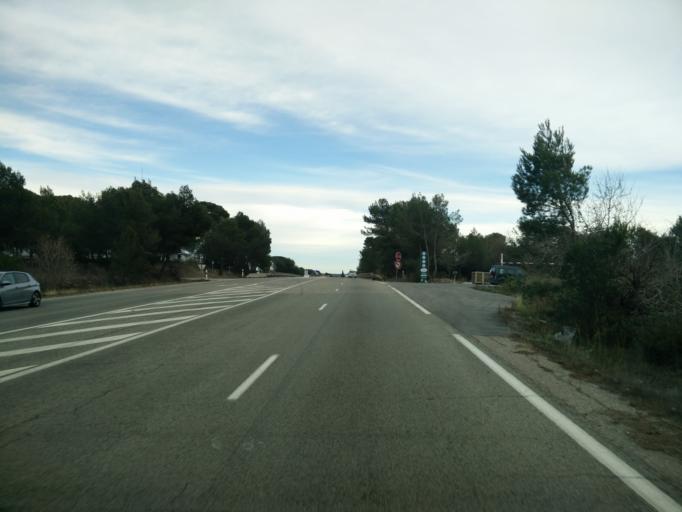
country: FR
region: Provence-Alpes-Cote d'Azur
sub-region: Departement du Var
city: Roquebrune-sur-Argens
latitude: 43.4646
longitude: 6.6215
